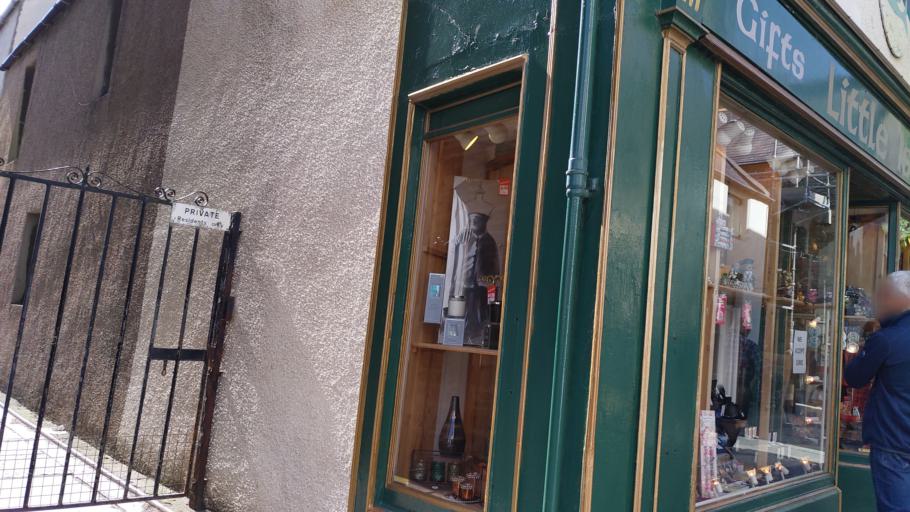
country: GB
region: Scotland
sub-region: Orkney Islands
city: Orkney
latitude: 58.9832
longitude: -2.9589
